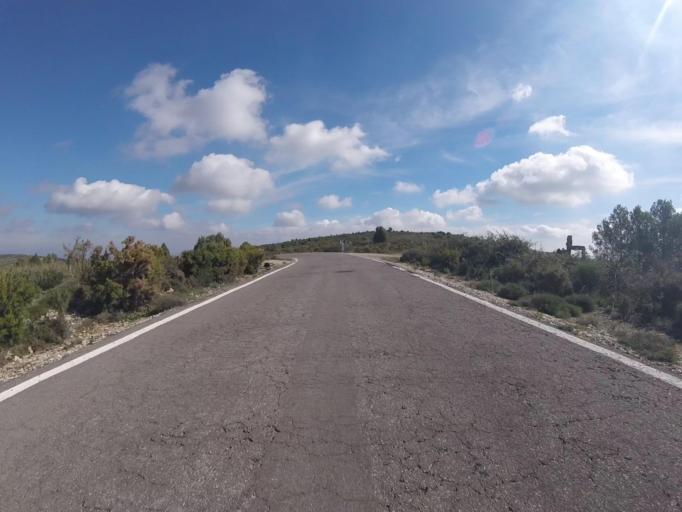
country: ES
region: Valencia
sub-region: Provincia de Castello
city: Albocasser
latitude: 40.3388
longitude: 0.0510
